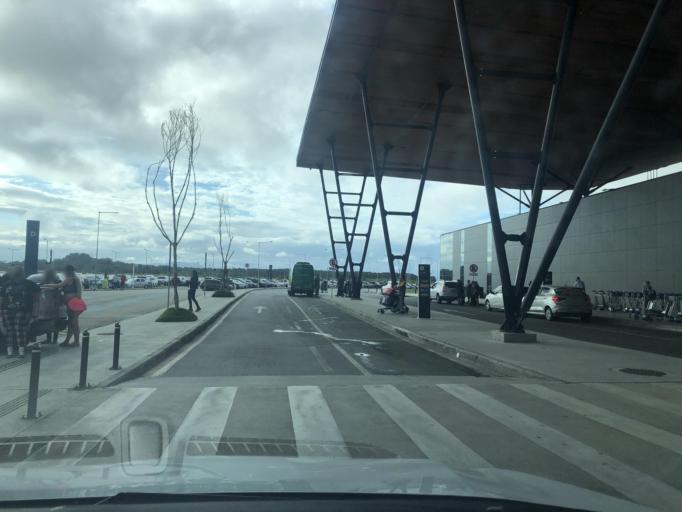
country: BR
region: Santa Catarina
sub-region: Florianopolis
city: Tapera
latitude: -27.6749
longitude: -48.5463
